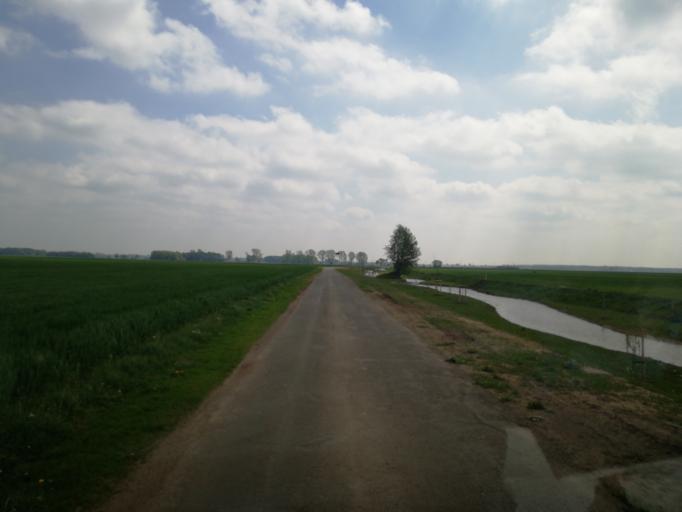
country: DE
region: Brandenburg
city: Doberlug-Kirchhain
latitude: 51.6865
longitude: 13.5321
